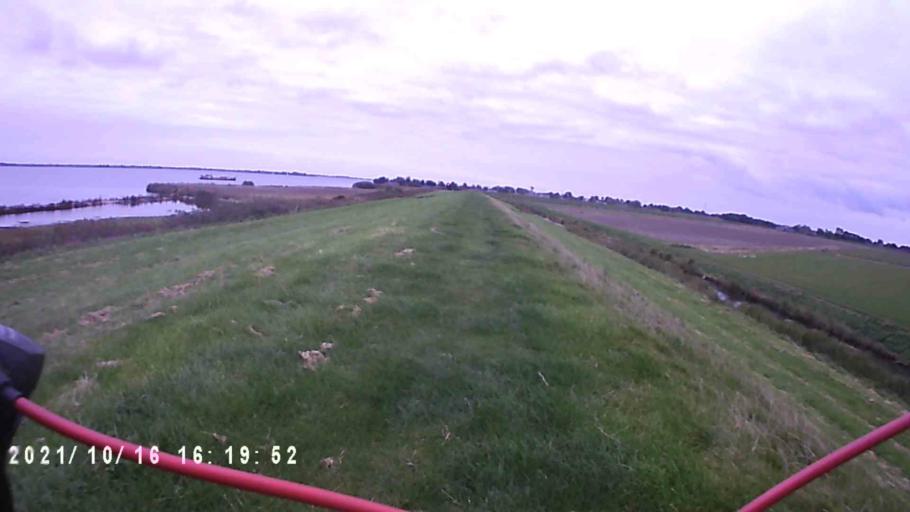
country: NL
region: Friesland
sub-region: Gemeente Dongeradeel
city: Anjum
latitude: 53.3897
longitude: 6.1543
